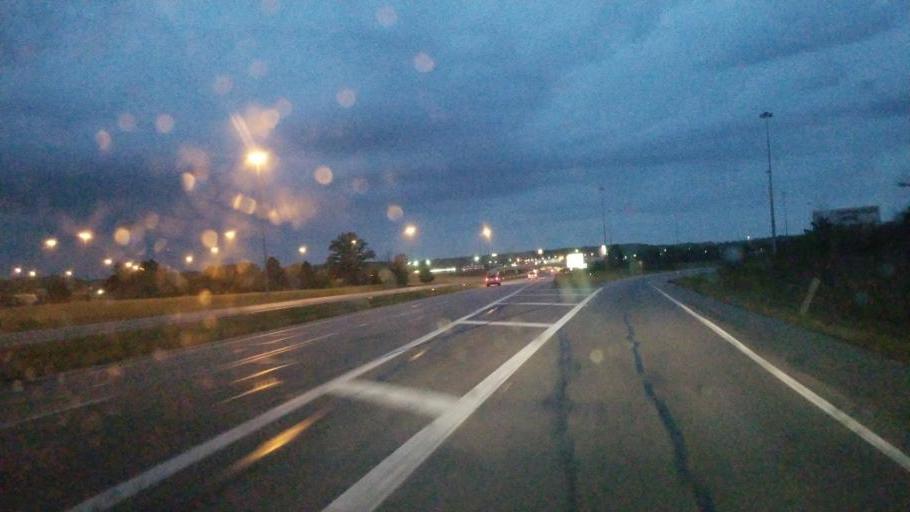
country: US
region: Ohio
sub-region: Medina County
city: Seville
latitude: 41.0308
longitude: -81.8932
